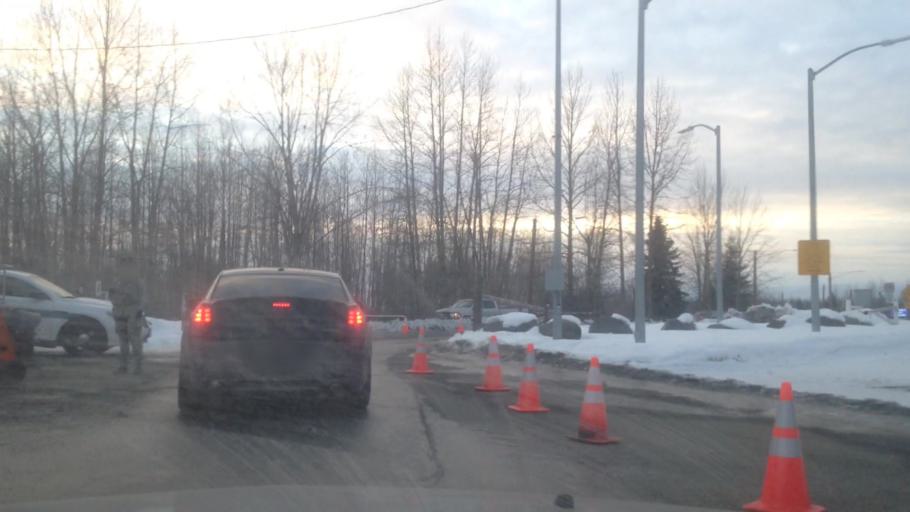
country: US
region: Alaska
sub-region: Anchorage Municipality
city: Elmendorf Air Force Base
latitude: 61.2576
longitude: -149.6632
